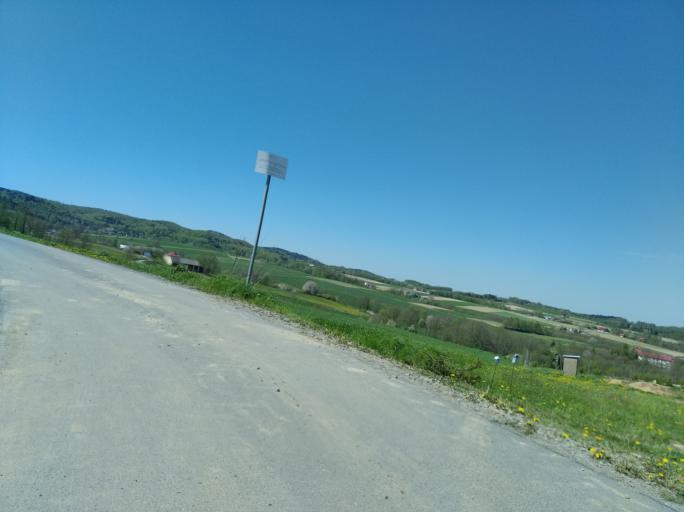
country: PL
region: Subcarpathian Voivodeship
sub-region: Powiat ropczycko-sedziszowski
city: Wielopole Skrzynskie
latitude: 49.9149
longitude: 21.5534
